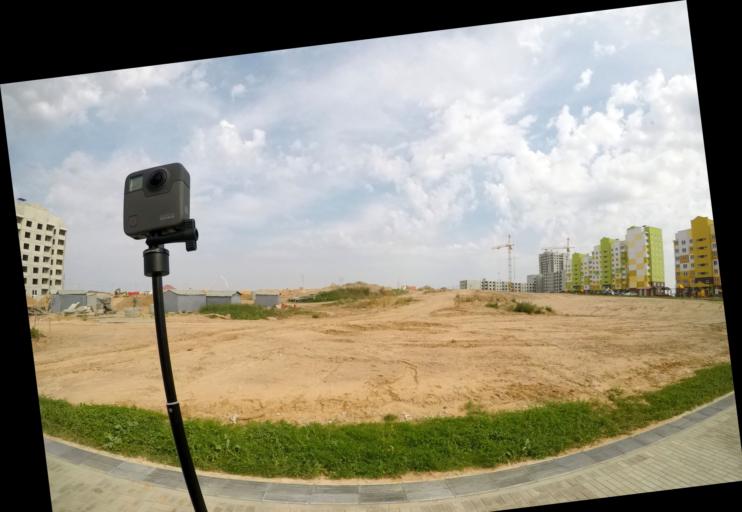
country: BY
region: Grodnenskaya
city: Hrodna
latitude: 53.7190
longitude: 23.8636
